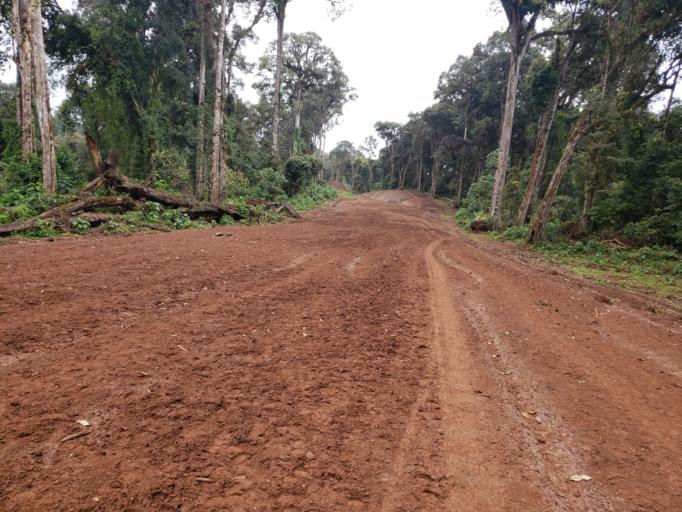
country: ET
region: Oromiya
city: Dodola
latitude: 6.5876
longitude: 39.4124
